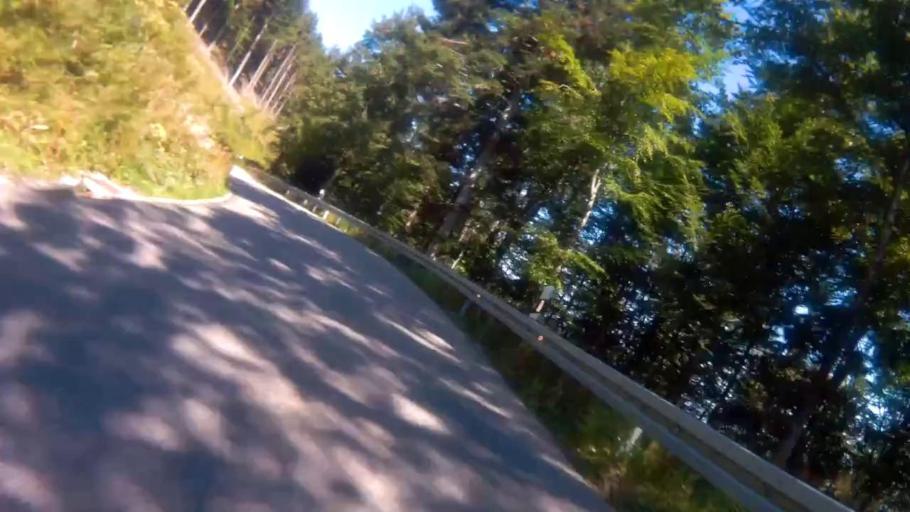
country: DE
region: Baden-Wuerttemberg
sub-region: Freiburg Region
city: Badenweiler
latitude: 47.7872
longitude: 7.7070
